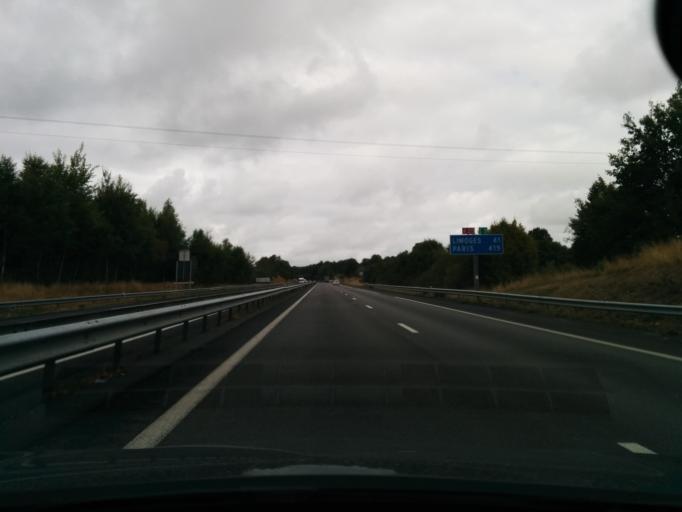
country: FR
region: Limousin
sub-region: Departement de la Haute-Vienne
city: Saint-Germain-les-Belles
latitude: 45.5490
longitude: 1.5082
